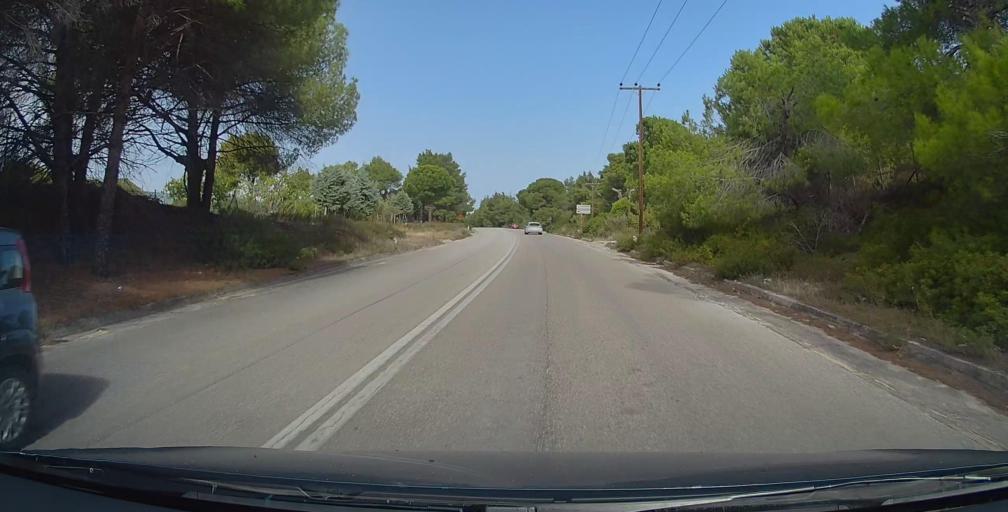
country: GR
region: Central Macedonia
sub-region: Nomos Chalkidikis
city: Sarti
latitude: 40.1227
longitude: 23.9686
